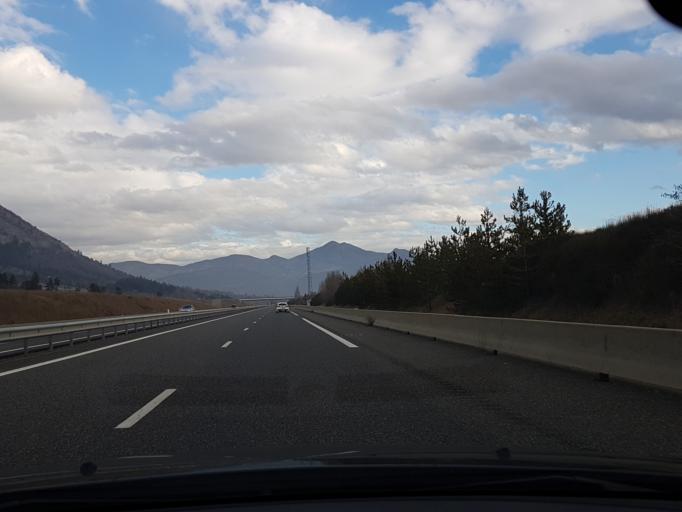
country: FR
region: Provence-Alpes-Cote d'Azur
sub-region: Departement des Hautes-Alpes
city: Tallard
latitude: 44.3887
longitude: 5.9388
